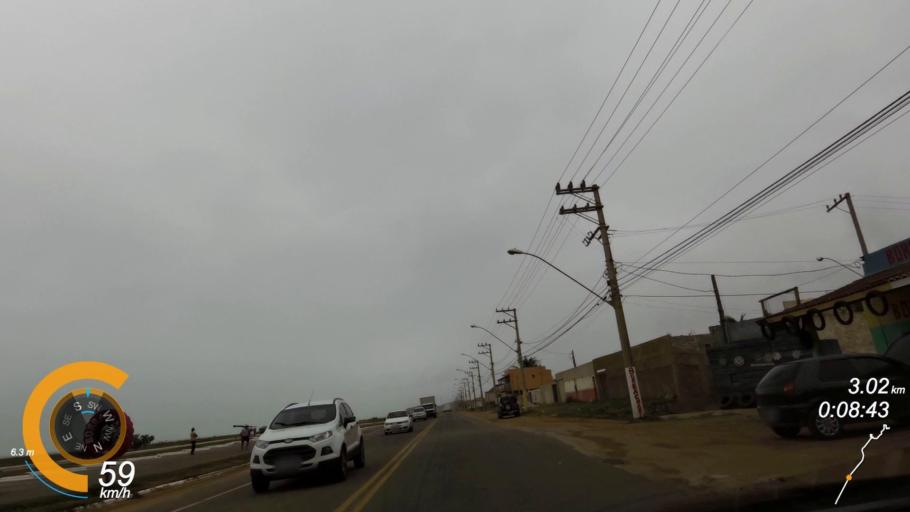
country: BR
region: Espirito Santo
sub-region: Guarapari
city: Guarapari
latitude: -20.6856
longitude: -40.5083
